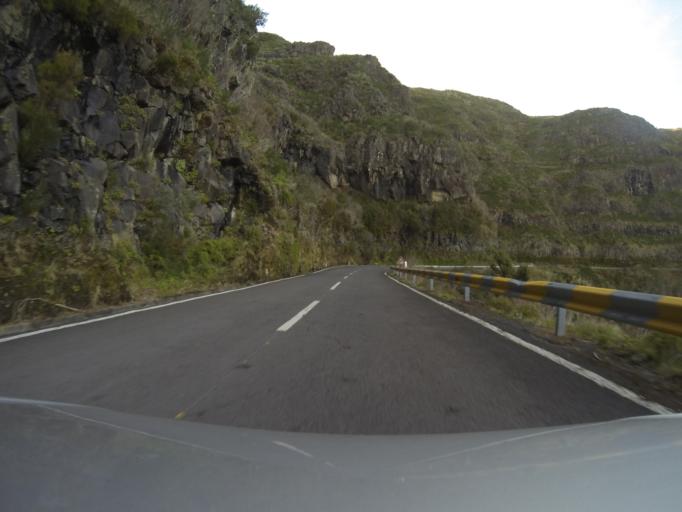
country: PT
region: Madeira
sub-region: Sao Vicente
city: Sao Vicente
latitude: 32.7392
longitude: -17.0503
